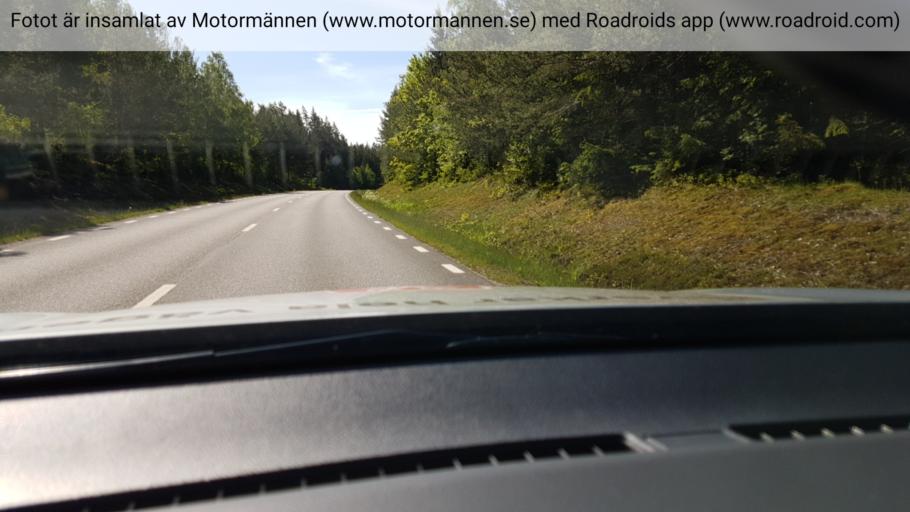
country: SE
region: Vaestra Goetaland
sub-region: Tibro Kommun
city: Tibro
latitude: 58.3940
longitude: 14.1999
